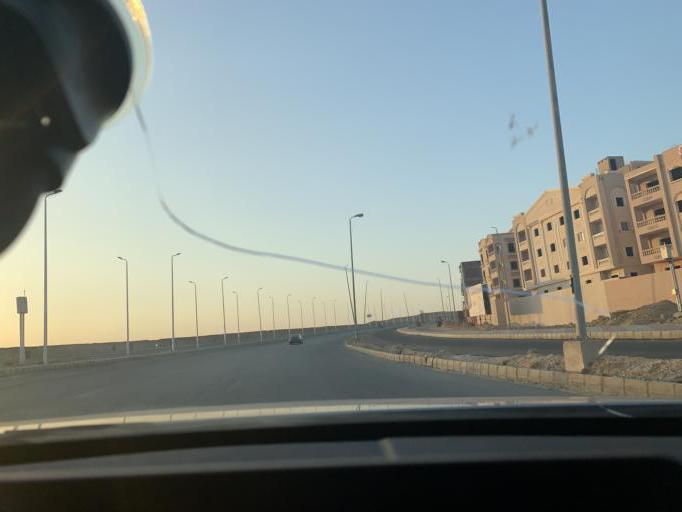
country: EG
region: Muhafazat al Qahirah
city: Halwan
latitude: 29.9772
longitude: 31.4695
